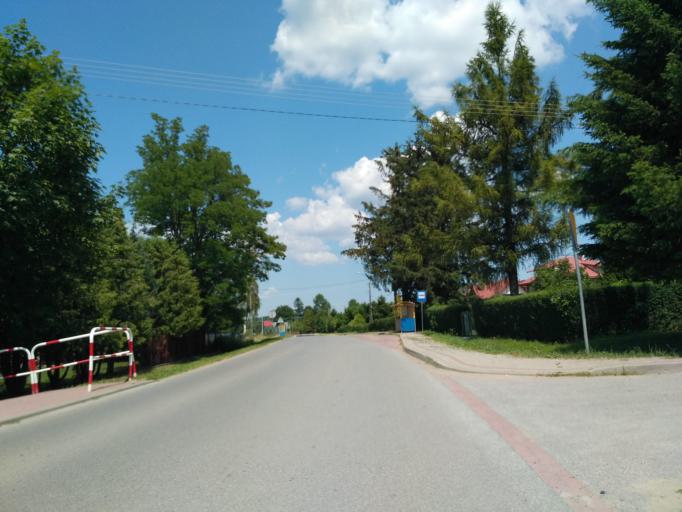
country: PL
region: Subcarpathian Voivodeship
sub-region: Powiat sanocki
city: Niebieszczany
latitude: 49.5274
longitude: 22.1280
